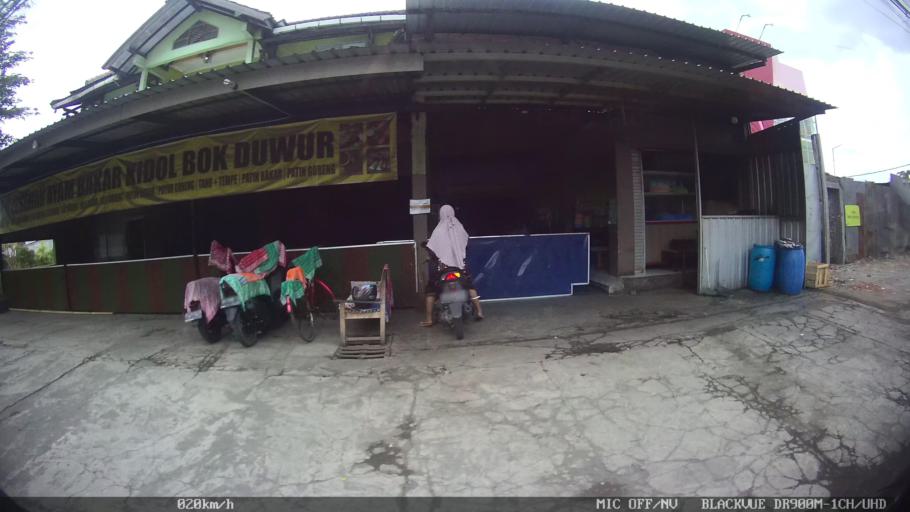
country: ID
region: Daerah Istimewa Yogyakarta
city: Sewon
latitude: -7.8404
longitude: 110.4114
